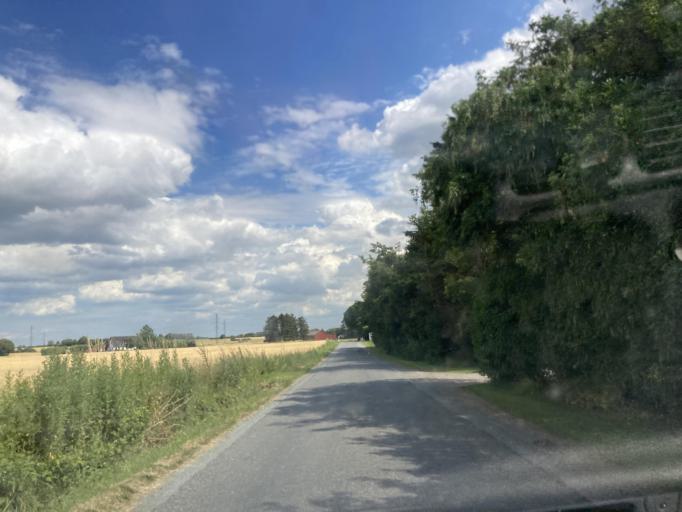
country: DK
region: Zealand
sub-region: Faxe Kommune
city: Haslev
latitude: 55.3568
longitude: 11.9750
